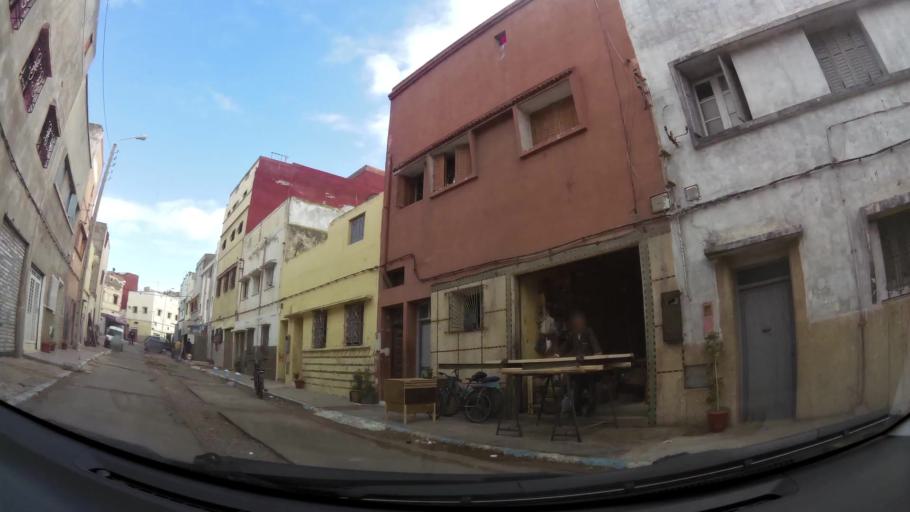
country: MA
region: Doukkala-Abda
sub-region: El-Jadida
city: El Jadida
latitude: 33.2589
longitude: -8.5147
